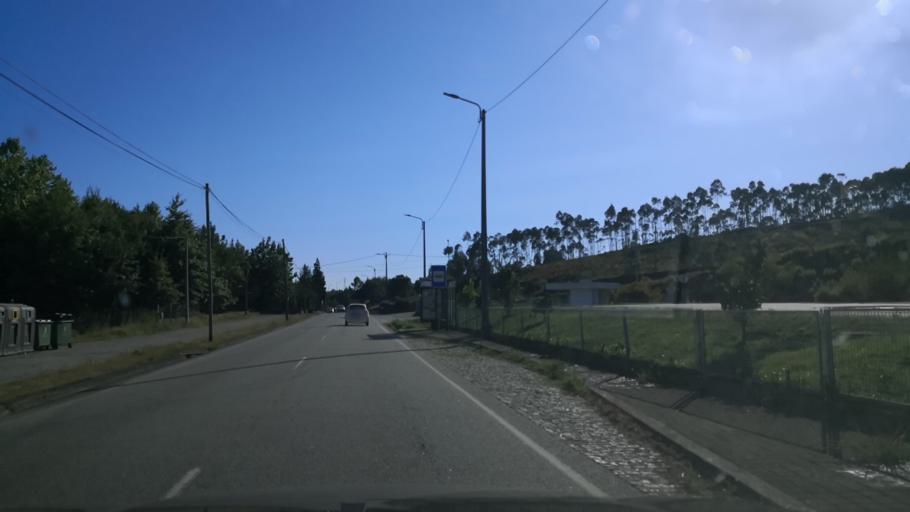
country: PT
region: Porto
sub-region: Pacos de Ferreira
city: Seroa
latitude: 41.2653
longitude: -8.4779
